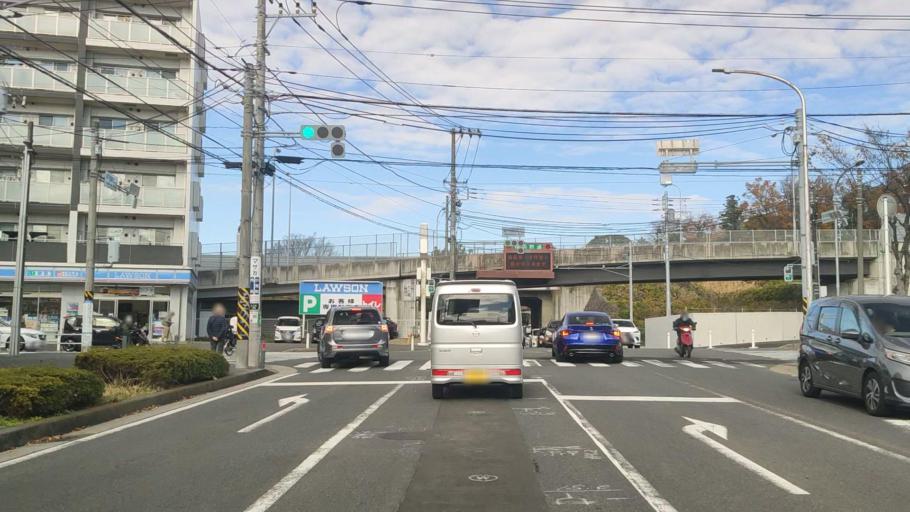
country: JP
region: Kanagawa
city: Yokohama
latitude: 35.4298
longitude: 139.5517
